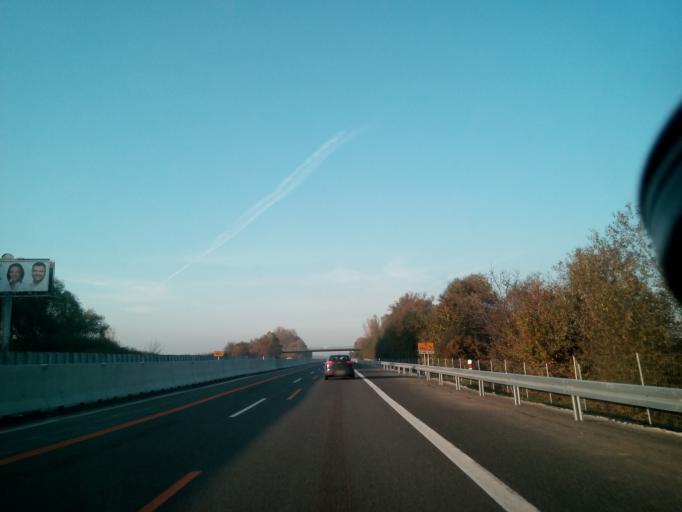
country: SK
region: Kosicky
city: Kosice
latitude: 48.7968
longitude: 21.3121
